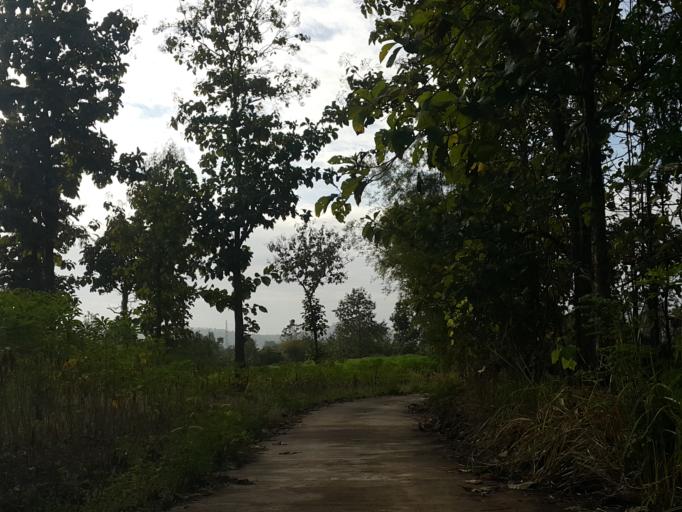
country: TH
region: Lampang
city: Mae Mo
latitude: 18.2616
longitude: 99.6025
